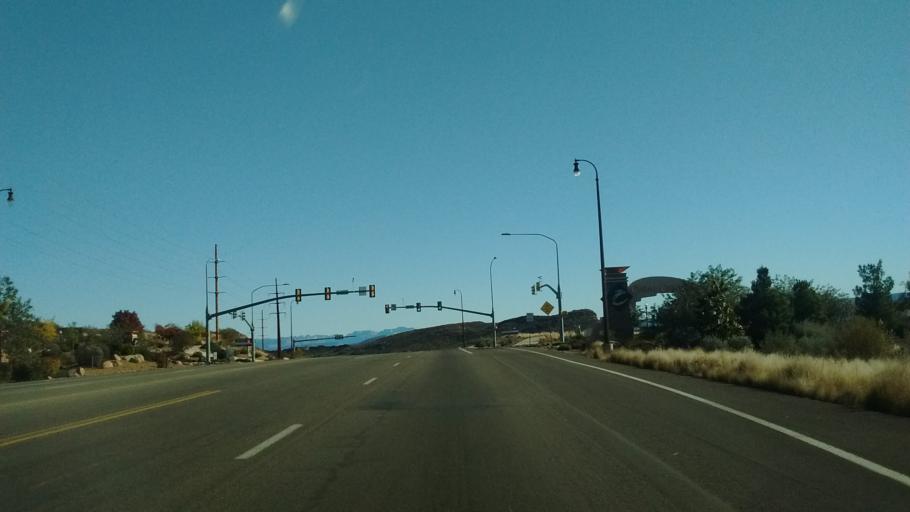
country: US
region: Utah
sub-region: Washington County
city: Washington
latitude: 37.1382
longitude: -113.4699
